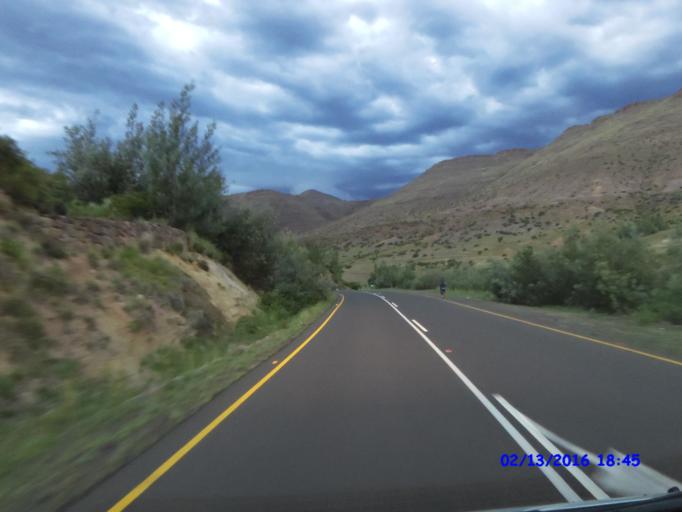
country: LS
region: Qacha's Nek
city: Qacha's Nek
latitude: -30.0547
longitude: 28.3038
